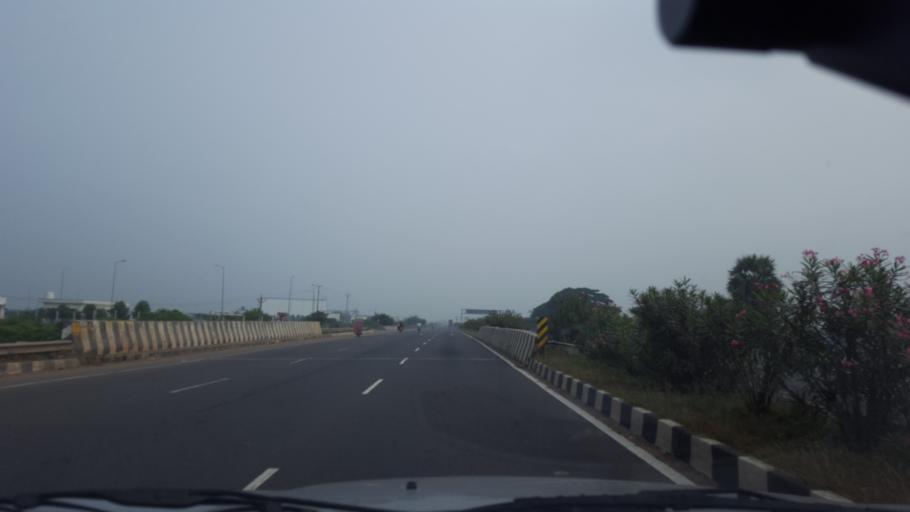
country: IN
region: Andhra Pradesh
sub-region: Guntur
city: Chilakalurupet
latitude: 16.0084
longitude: 80.1158
